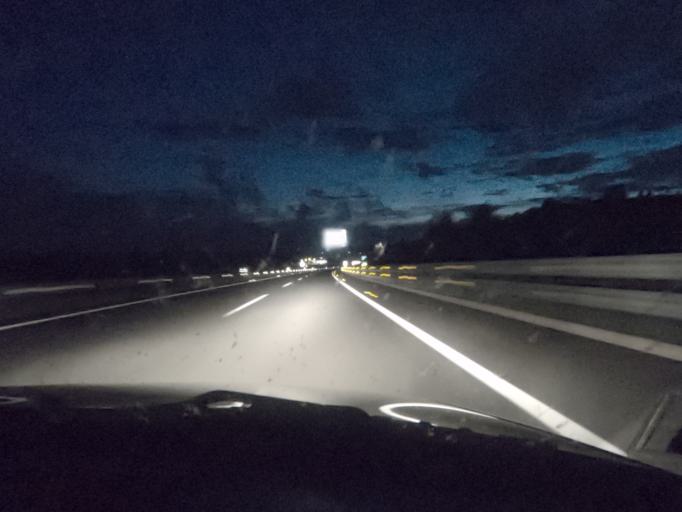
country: ES
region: Extremadura
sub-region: Provincia de Caceres
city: Coria
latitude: 39.9845
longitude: -6.4892
